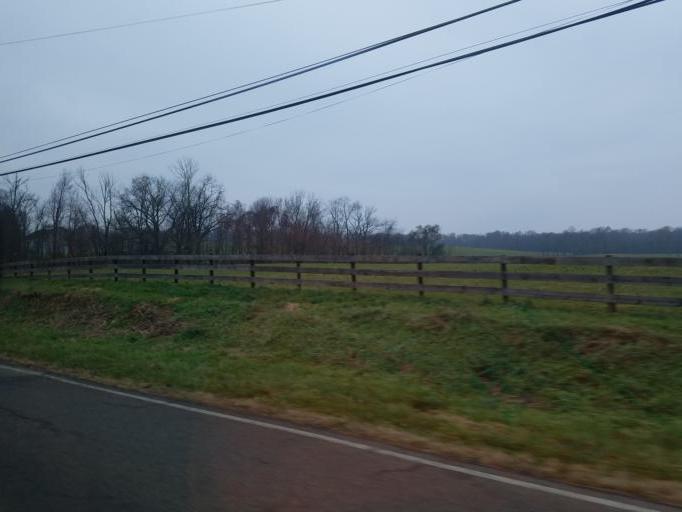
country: US
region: Ohio
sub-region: Richland County
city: Mansfield
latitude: 40.7082
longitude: -82.5116
